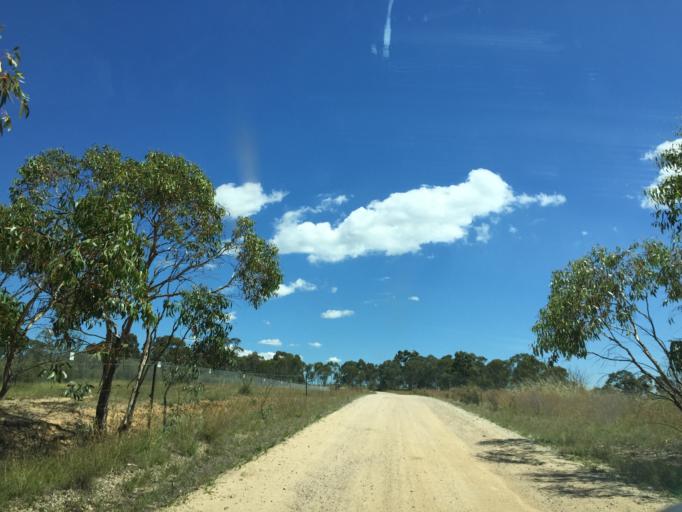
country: AU
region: New South Wales
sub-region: Lithgow
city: Lithgow
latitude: -33.4343
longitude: 150.1331
